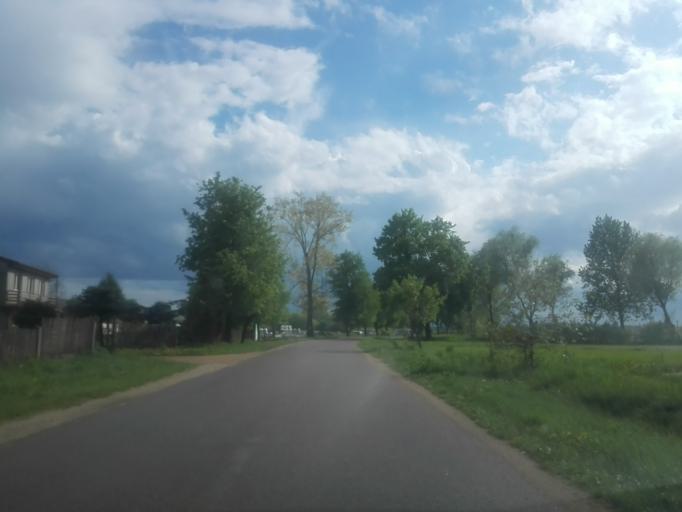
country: PL
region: Podlasie
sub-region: Powiat lomzynski
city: Wizna
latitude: 53.2426
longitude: 22.4346
